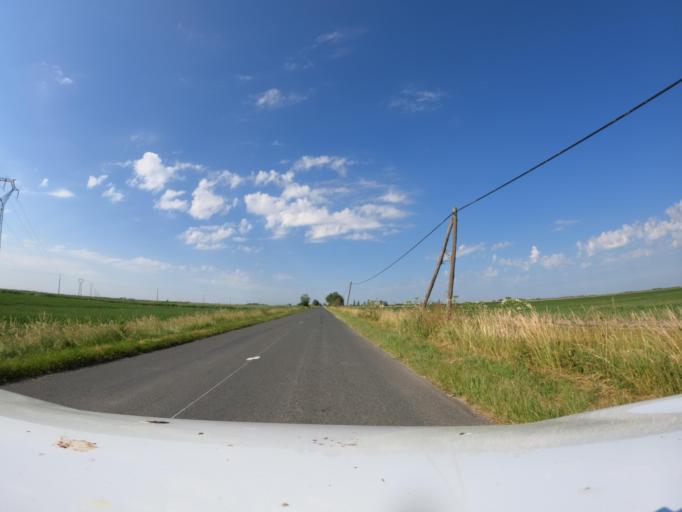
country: FR
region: Pays de la Loire
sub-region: Departement de la Vendee
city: Champagne-les-Marais
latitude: 46.3665
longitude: -1.1085
